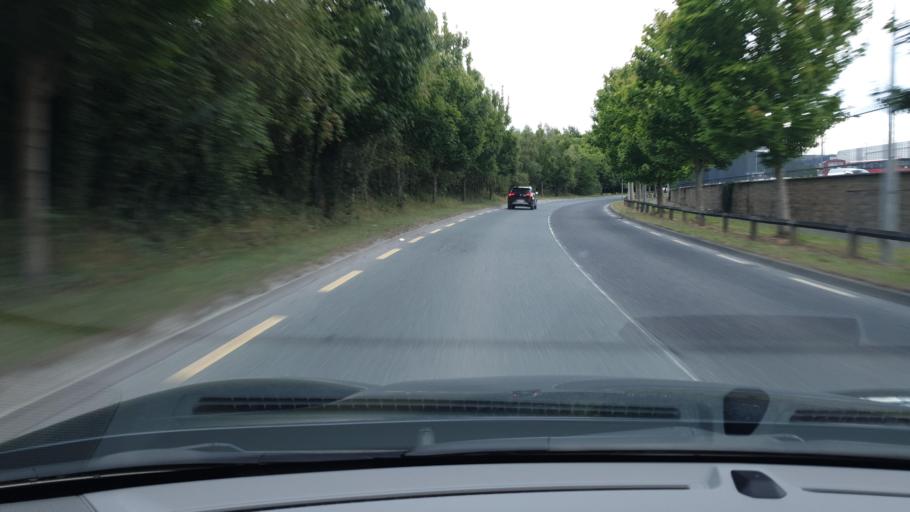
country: IE
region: Leinster
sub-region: South Dublin
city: Saggart
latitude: 53.2958
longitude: -6.4387
